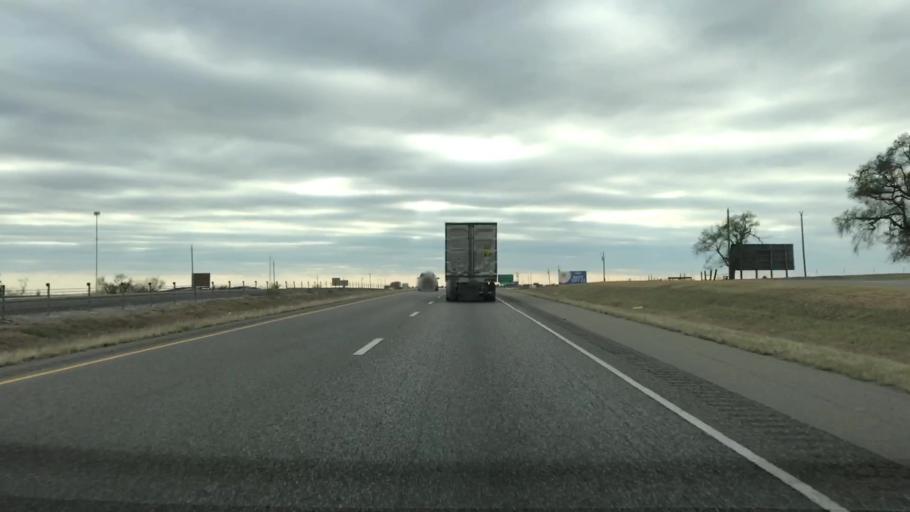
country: US
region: Oklahoma
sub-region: Beckham County
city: Sayre
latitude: 35.3262
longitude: -99.6050
